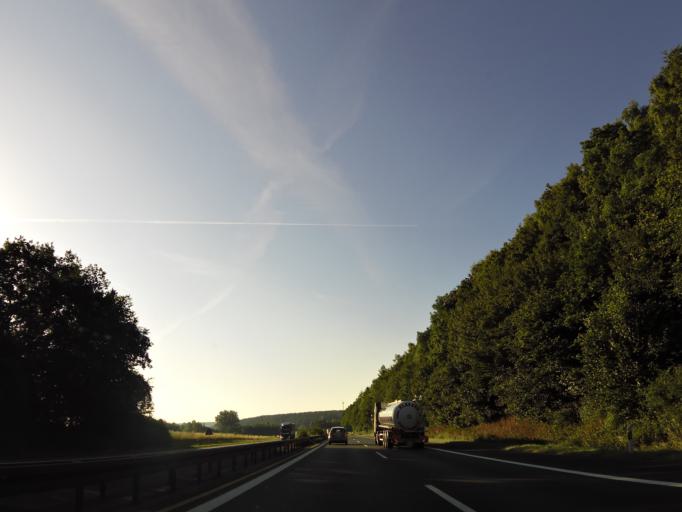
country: DE
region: Bavaria
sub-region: Upper Franconia
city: Schlusselfeld
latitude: 49.7470
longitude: 10.6249
